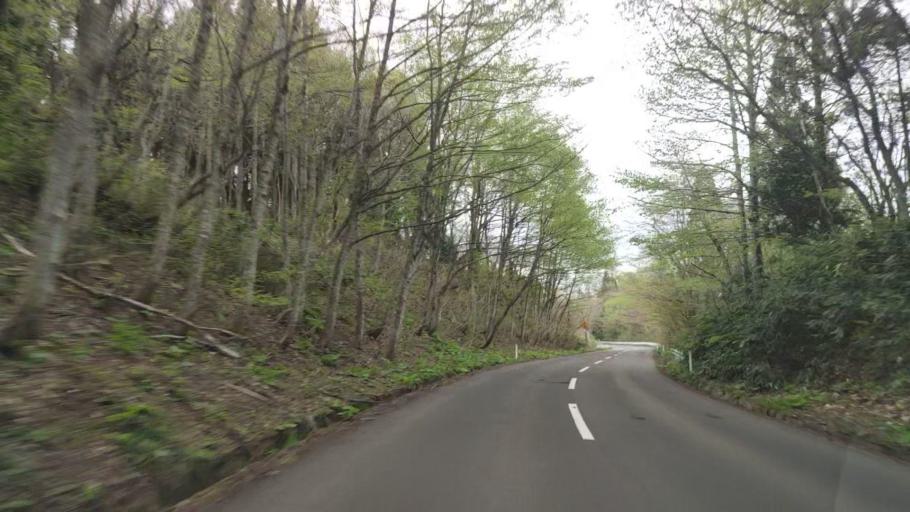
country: JP
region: Akita
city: Hanawa
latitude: 40.3784
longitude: 140.7912
